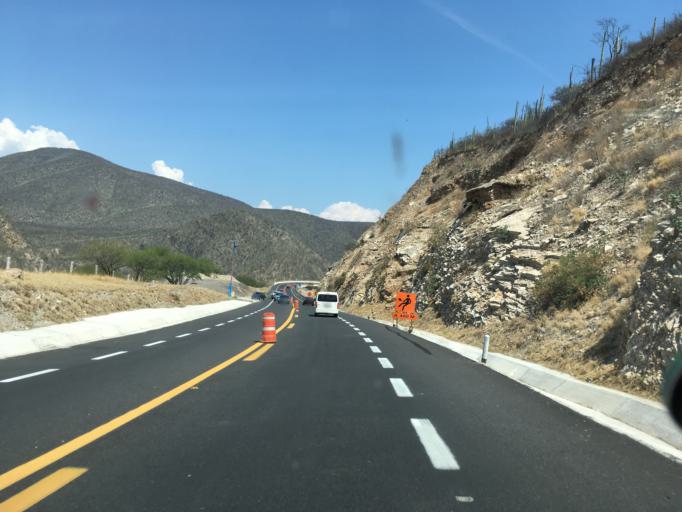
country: MX
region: Puebla
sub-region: San Jose Miahuatlan
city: San Pedro Tetitlan
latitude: 18.1662
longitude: -97.2639
